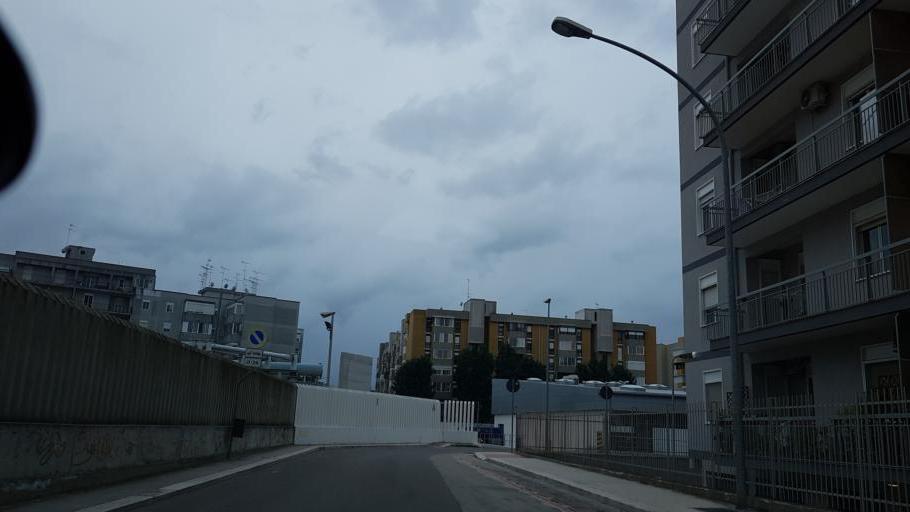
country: IT
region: Apulia
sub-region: Provincia di Brindisi
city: Brindisi
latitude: 40.6270
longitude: 17.9234
